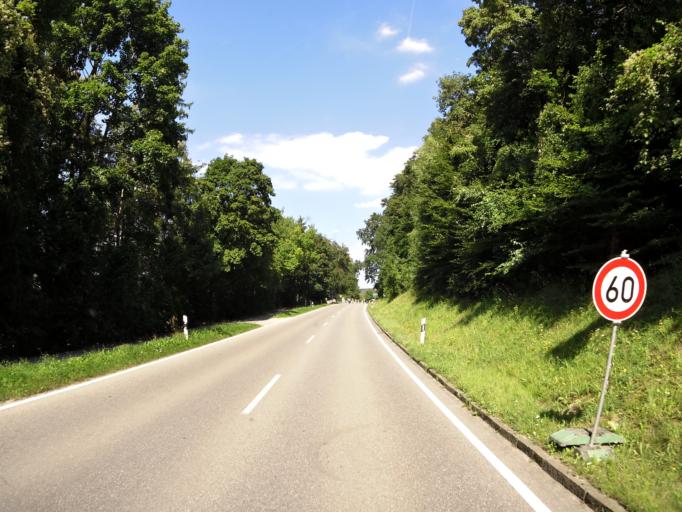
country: DE
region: Bavaria
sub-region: Upper Bavaria
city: Herrsching am Ammersee
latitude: 47.9829
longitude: 11.1610
